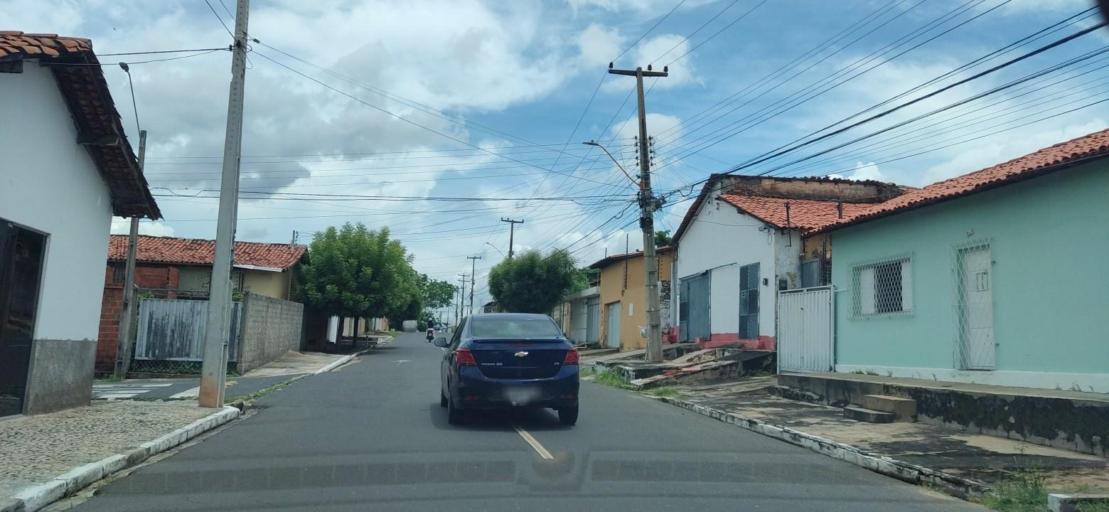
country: BR
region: Piaui
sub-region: Teresina
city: Teresina
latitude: -5.0742
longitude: -42.8047
